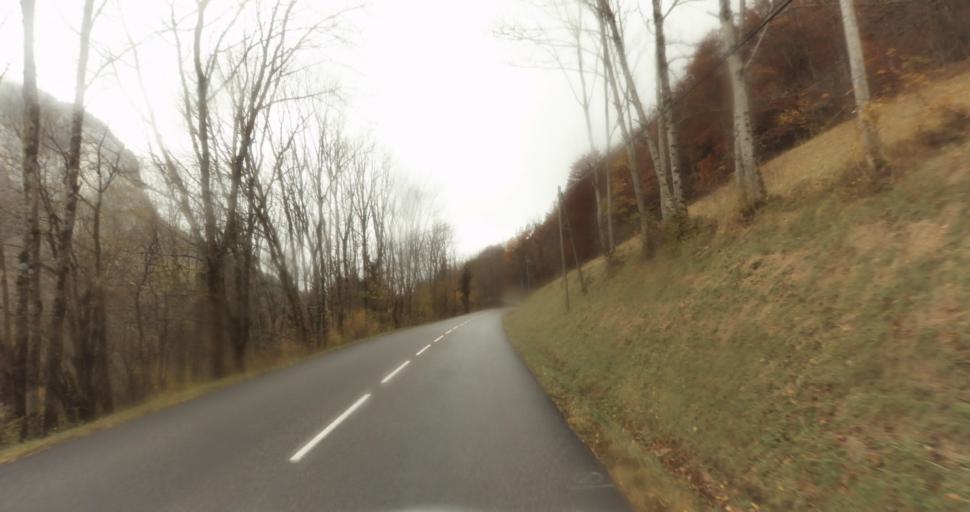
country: FR
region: Rhone-Alpes
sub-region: Departement de la Haute-Savoie
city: Thorens-Glieres
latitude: 45.9881
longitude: 6.2706
